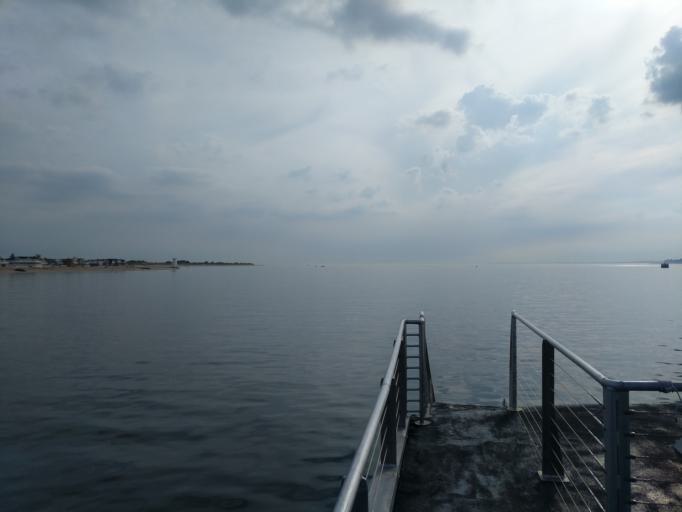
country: US
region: New York
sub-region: Kings County
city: Coney Island
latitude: 40.5653
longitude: -73.9210
